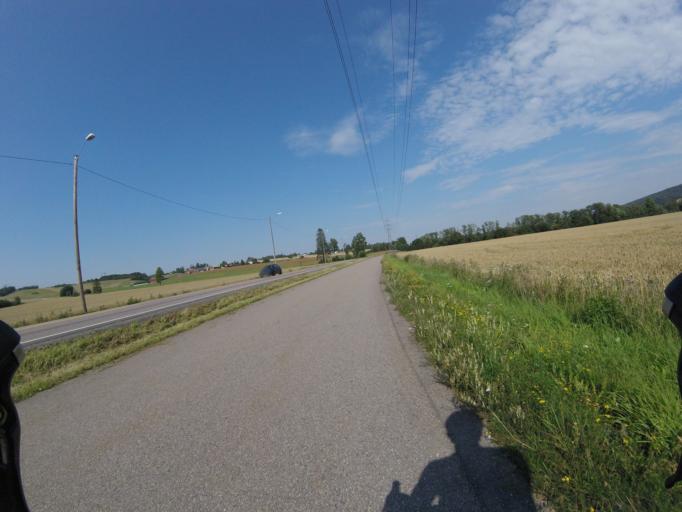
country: NO
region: Akershus
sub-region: Skedsmo
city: Leirsund
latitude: 59.9865
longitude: 11.0725
